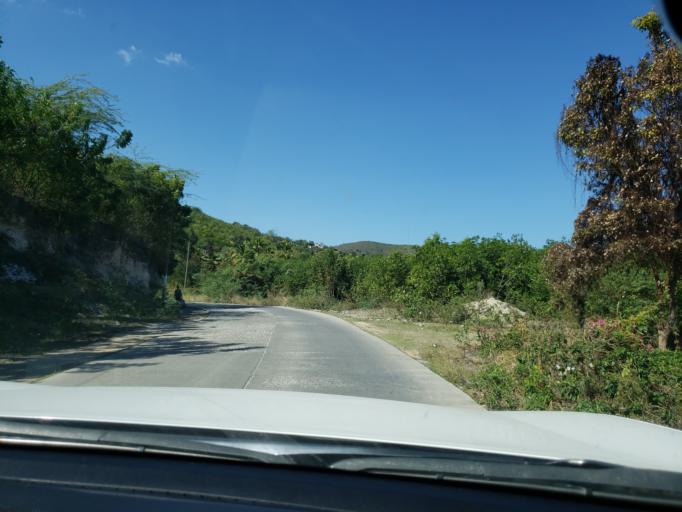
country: HT
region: Nippes
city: Miragoane
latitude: 18.4452
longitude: -73.1026
